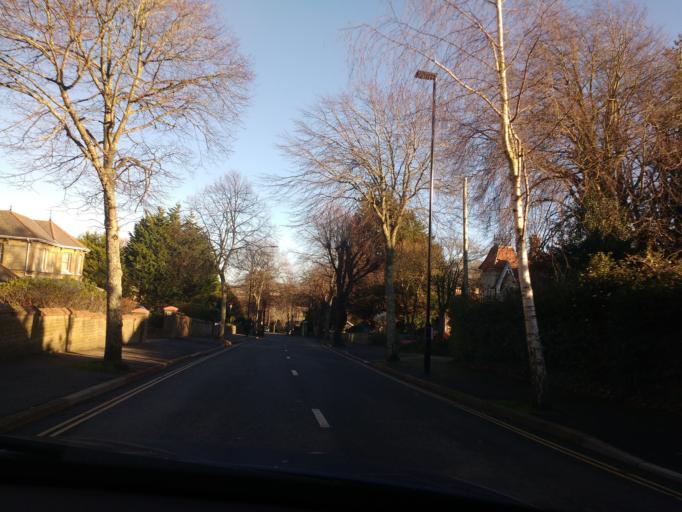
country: GB
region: England
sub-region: Isle of Wight
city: Shanklin
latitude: 50.6274
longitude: -1.1876
